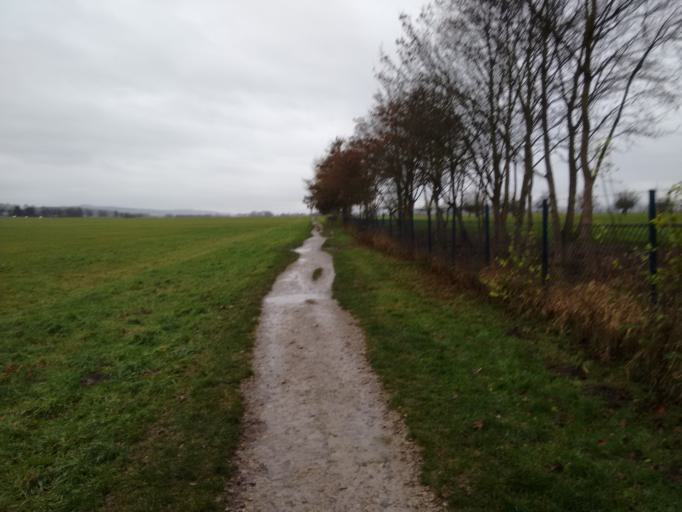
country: DE
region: Lower Saxony
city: Goettingen
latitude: 51.5125
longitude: 9.9350
